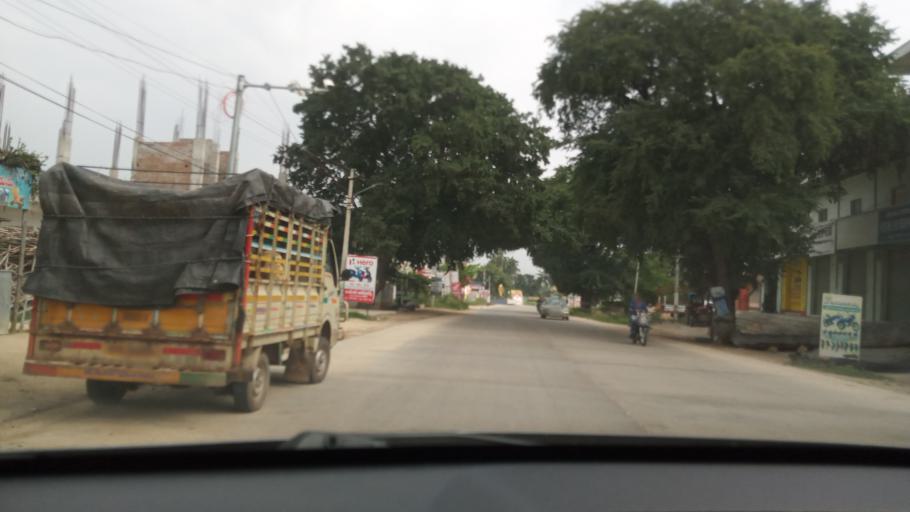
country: IN
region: Andhra Pradesh
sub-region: Chittoor
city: Madanapalle
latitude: 13.6527
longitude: 78.8070
